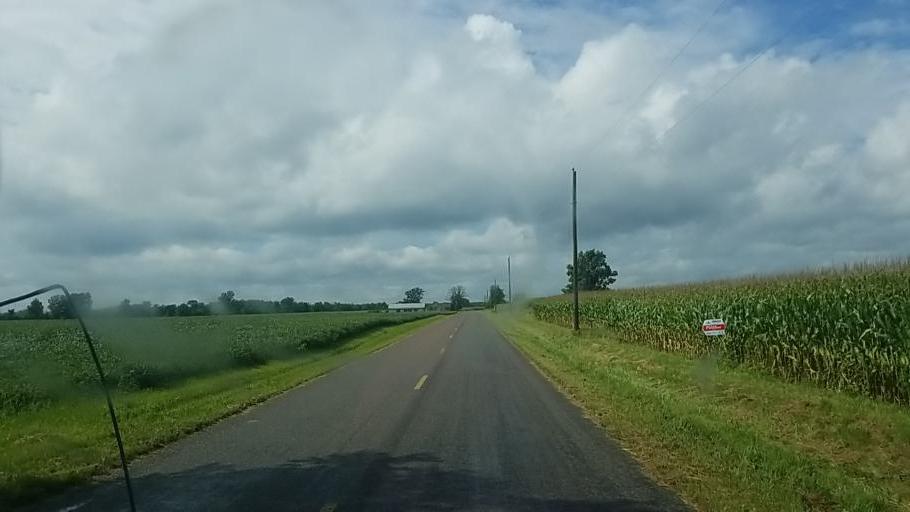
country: US
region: Ohio
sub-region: Hardin County
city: Kenton
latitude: 40.4884
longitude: -83.5162
